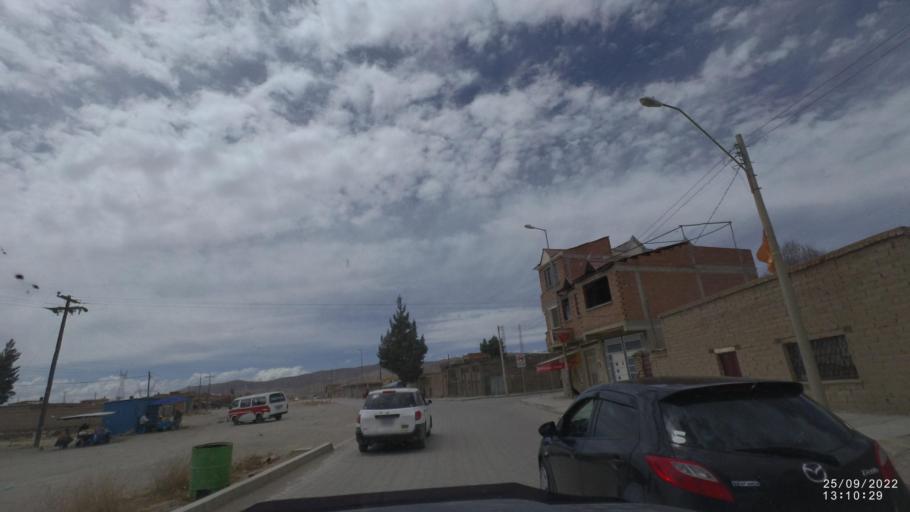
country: BO
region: Oruro
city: Oruro
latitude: -17.9712
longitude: -67.0487
